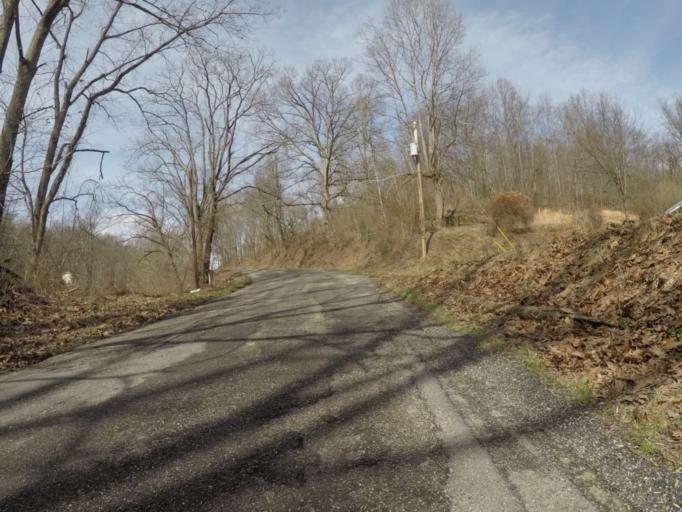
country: US
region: Ohio
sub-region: Lawrence County
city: Burlington
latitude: 38.4841
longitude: -82.5348
